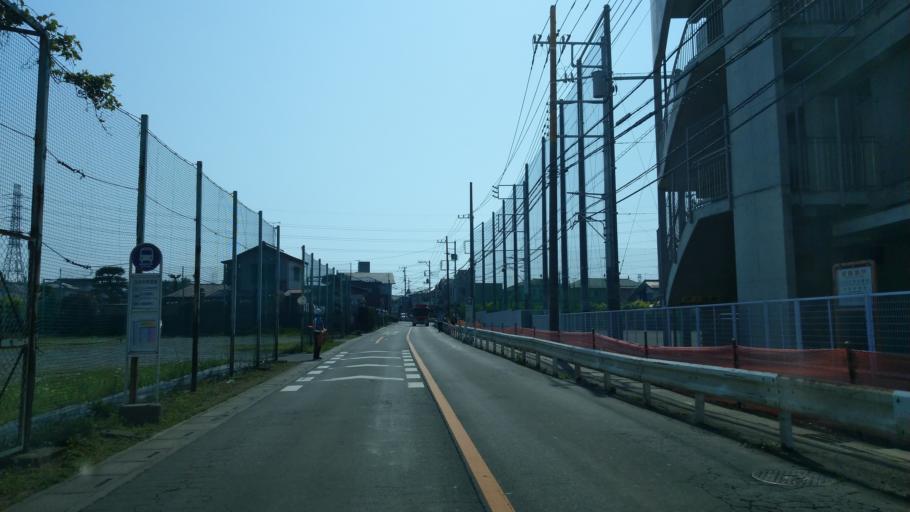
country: JP
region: Saitama
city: Oi
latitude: 35.8523
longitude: 139.5123
